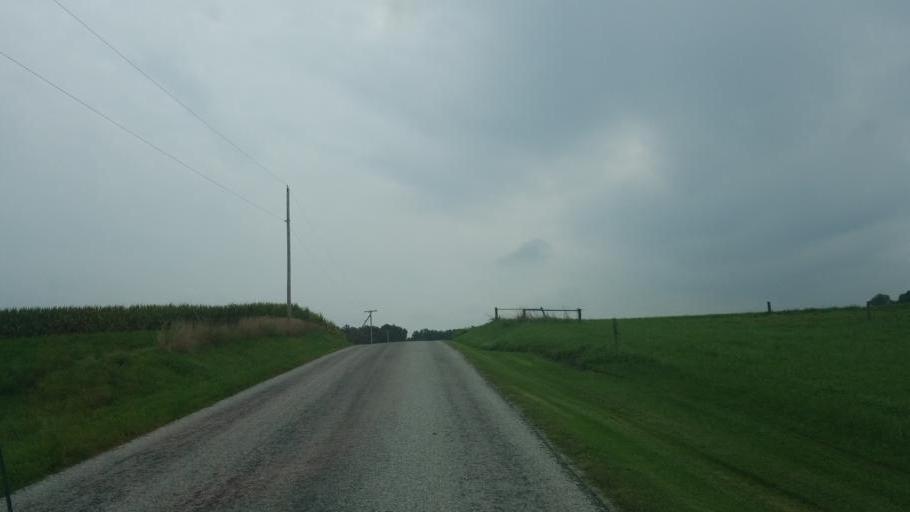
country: US
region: Ohio
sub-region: Wayne County
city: Creston
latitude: 40.9362
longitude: -81.8504
